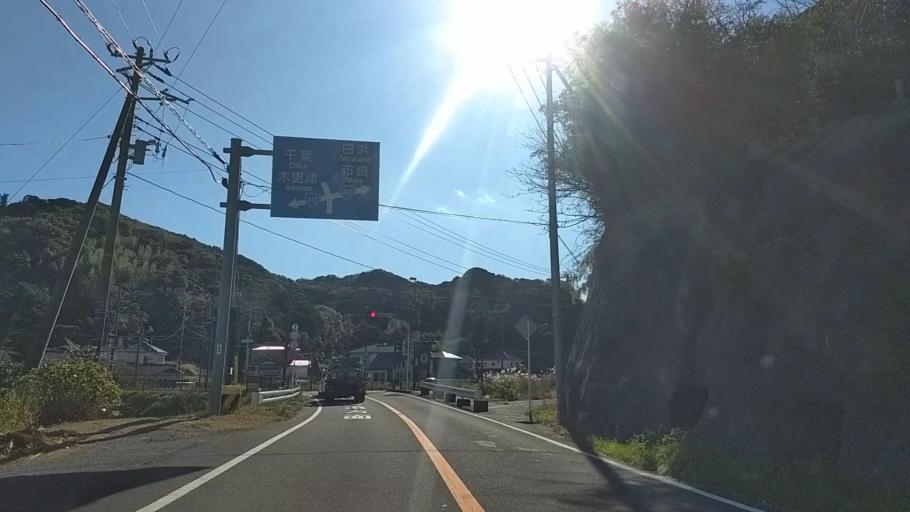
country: JP
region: Chiba
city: Tateyama
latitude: 34.9739
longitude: 139.8639
